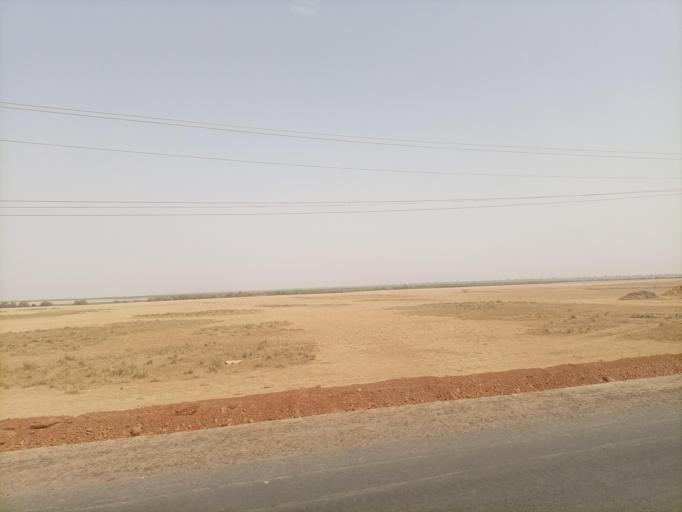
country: SN
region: Fatick
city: Foundiougne
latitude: 14.1502
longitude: -16.4710
